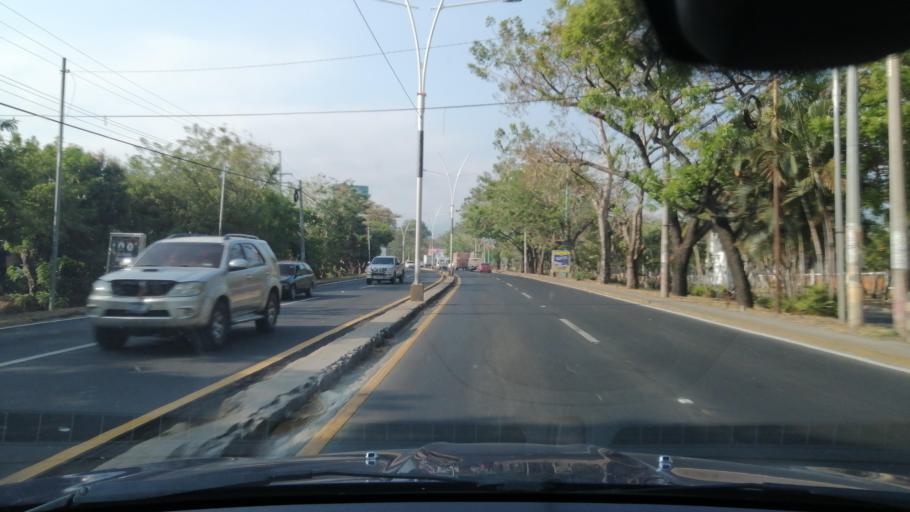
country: SV
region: Santa Ana
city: Santa Ana
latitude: 13.9737
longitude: -89.5629
